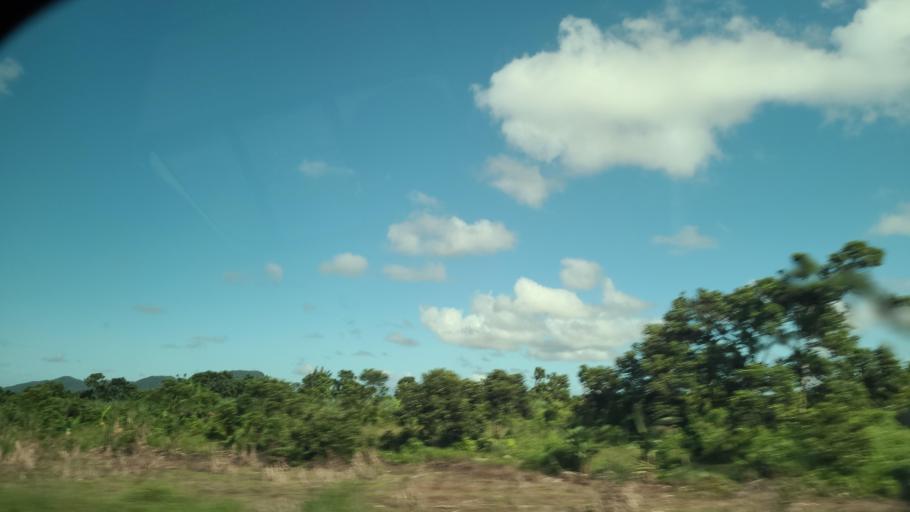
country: MU
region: Flacq
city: Saint Julien
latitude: -20.2365
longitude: 57.6292
